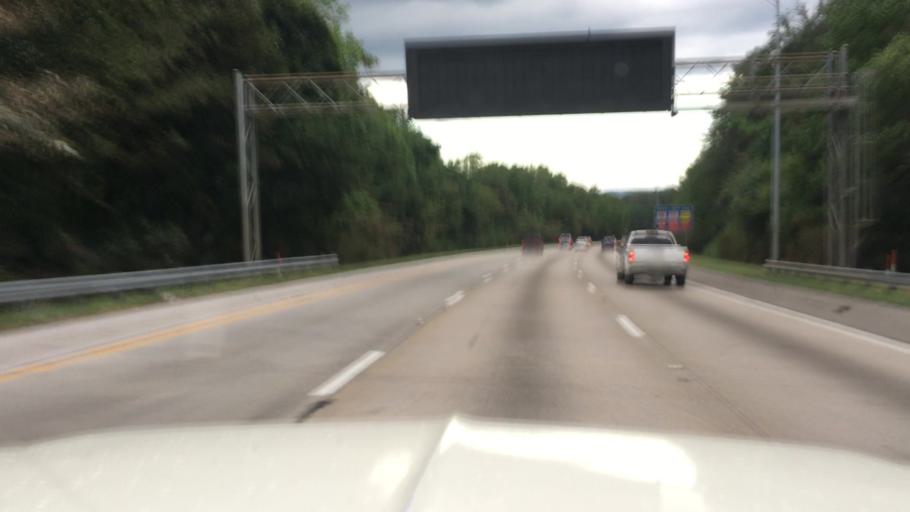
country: US
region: Alabama
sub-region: Jefferson County
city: Hoover
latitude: 33.4247
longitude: -86.8170
